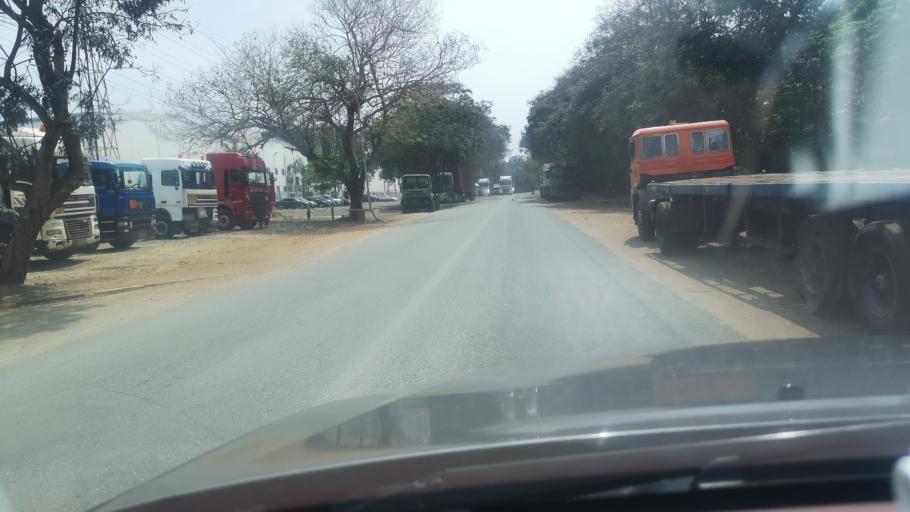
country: GH
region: Greater Accra
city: Tema
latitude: 5.6244
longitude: -0.0184
